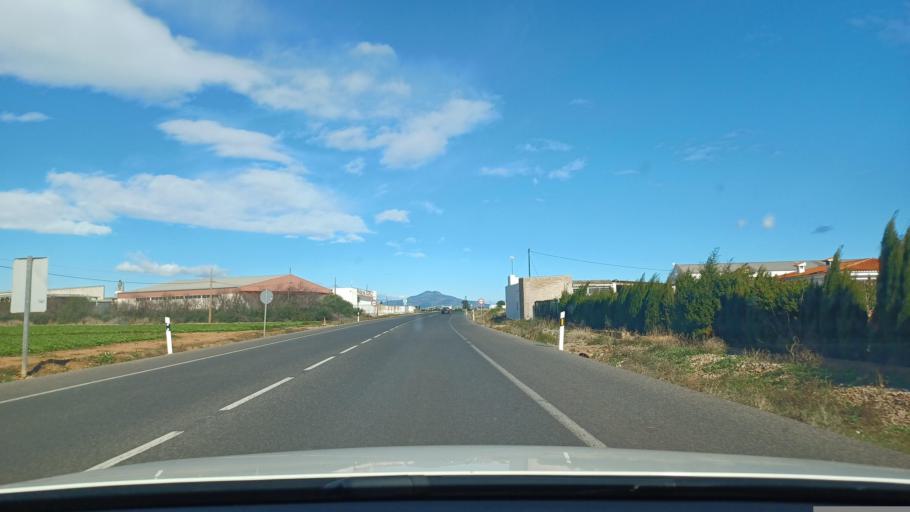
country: ES
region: Valencia
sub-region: Provincia de Castello
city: Benicarlo
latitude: 40.4365
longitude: 0.4400
